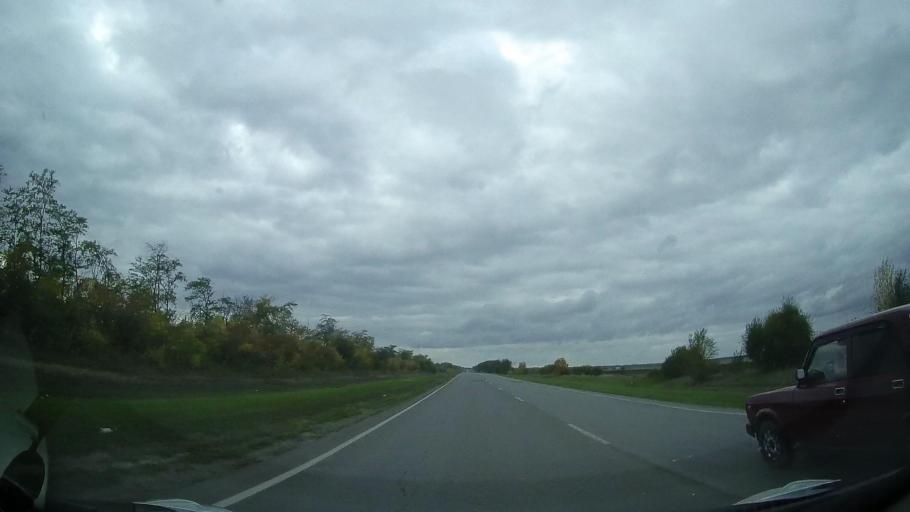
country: RU
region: Rostov
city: Yegorlykskaya
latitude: 46.5480
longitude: 40.7450
